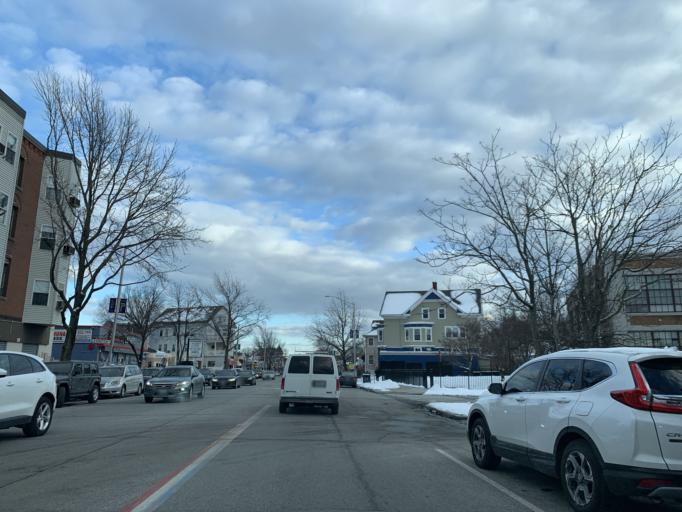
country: US
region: Rhode Island
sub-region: Providence County
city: Providence
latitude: 41.8002
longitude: -71.4172
